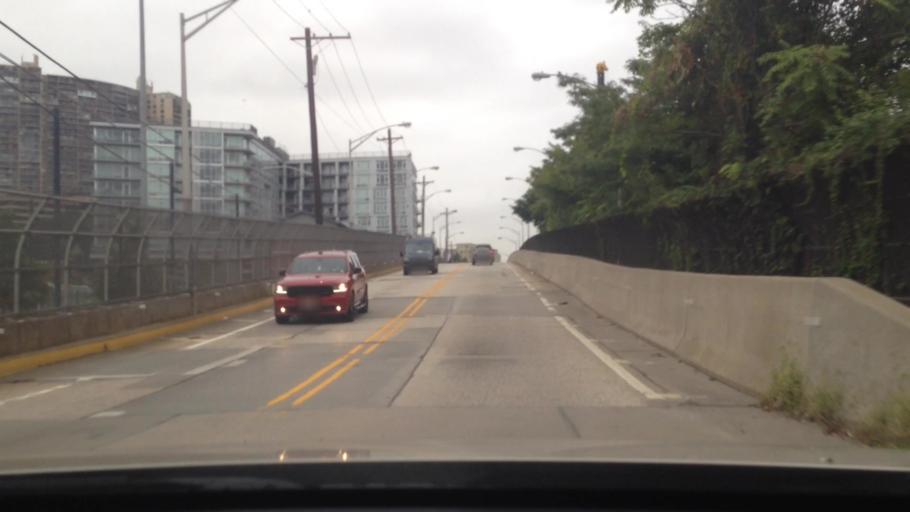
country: US
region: New Jersey
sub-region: Hudson County
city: Hoboken
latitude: 40.7566
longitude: -74.0279
